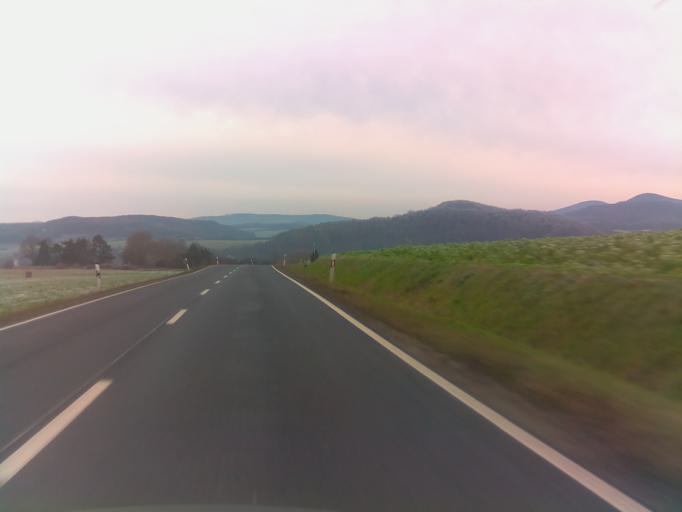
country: DE
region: Thuringia
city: Buttlar
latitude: 50.7731
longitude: 9.9702
